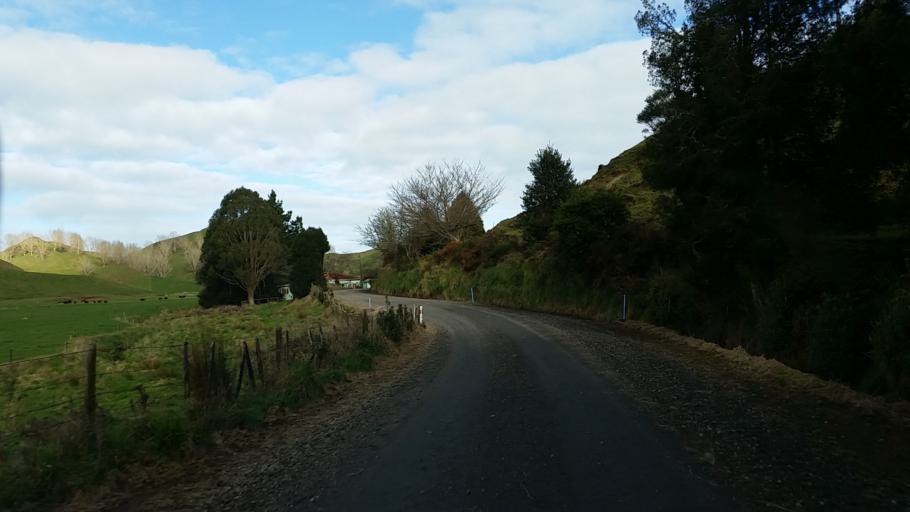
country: NZ
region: Taranaki
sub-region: South Taranaki District
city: Eltham
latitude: -39.2519
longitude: 174.5336
